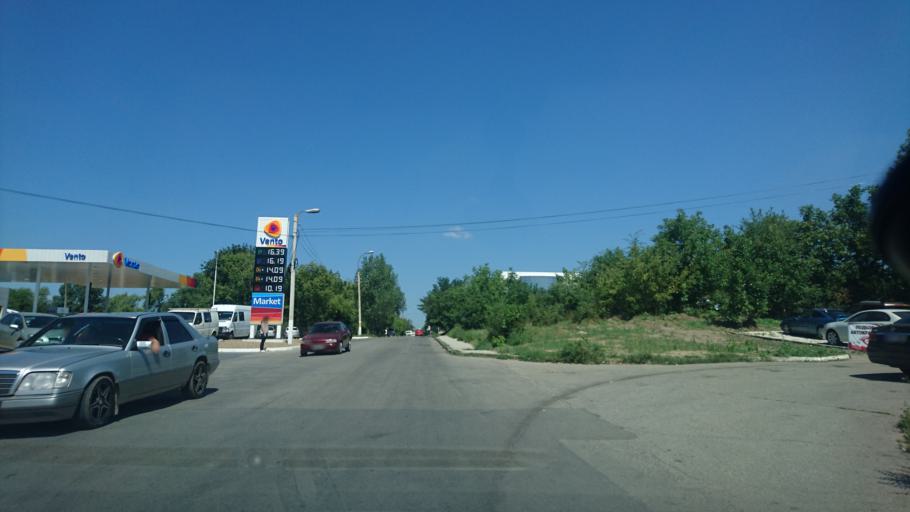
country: MD
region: Laloveni
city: Ialoveni
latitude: 46.9940
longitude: 28.7870
